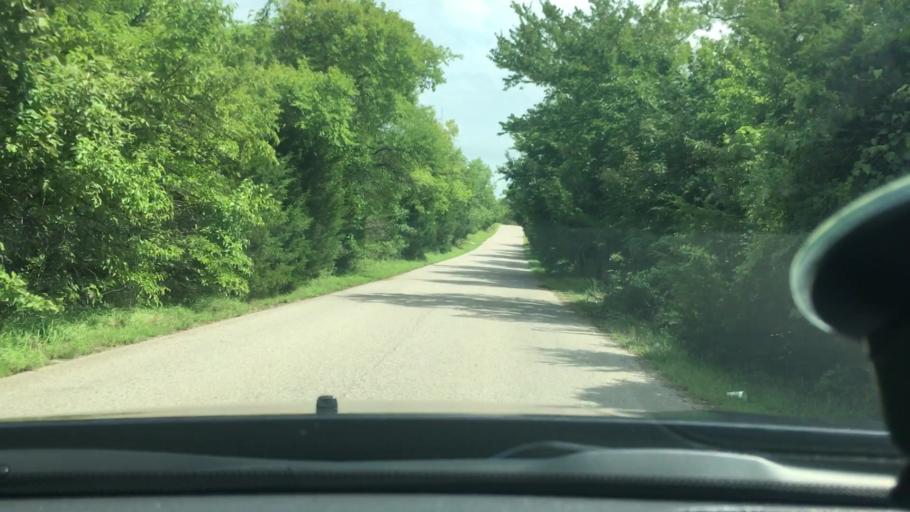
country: US
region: Oklahoma
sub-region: Pontotoc County
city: Ada
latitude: 34.8080
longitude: -96.7007
